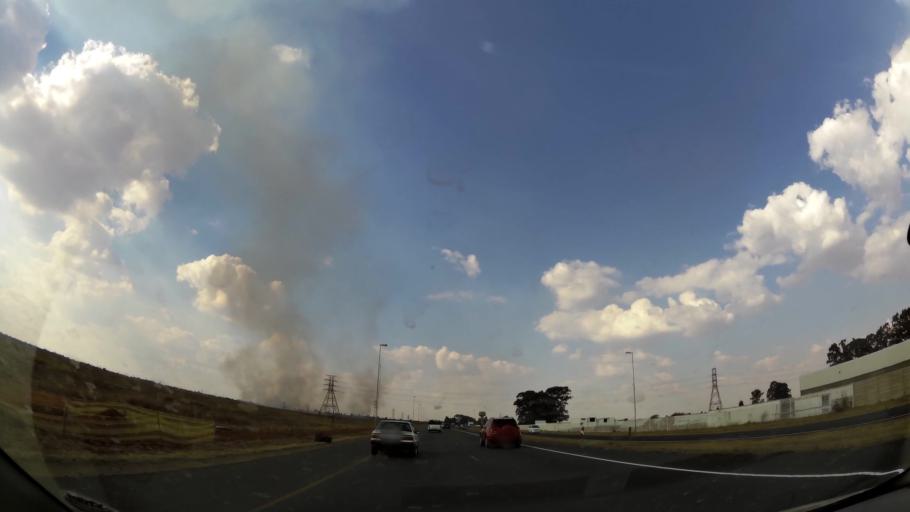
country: ZA
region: Gauteng
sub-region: Ekurhuleni Metropolitan Municipality
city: Boksburg
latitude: -26.2741
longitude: 28.2759
